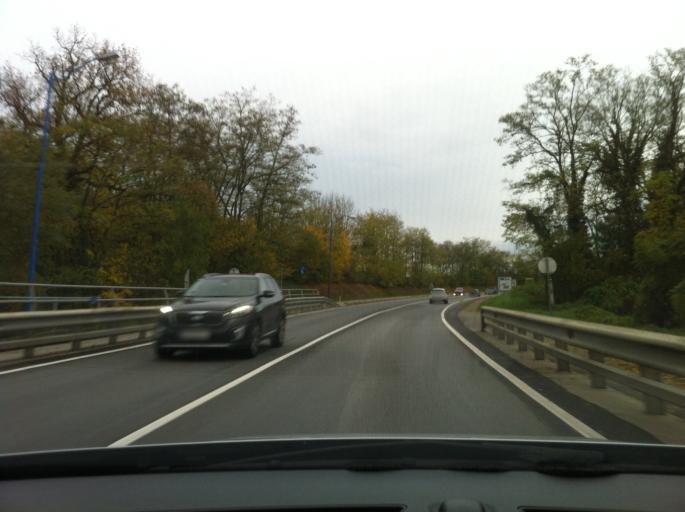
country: AT
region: Lower Austria
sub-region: Politischer Bezirk Melk
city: Emmersdorf an der Donau
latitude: 48.2393
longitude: 15.3481
